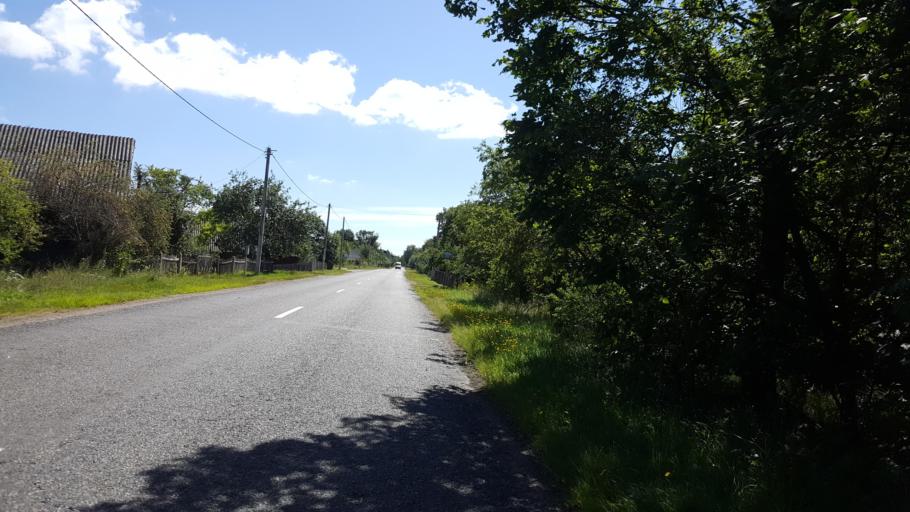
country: BY
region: Brest
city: Zhabinka
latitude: 52.3668
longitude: 24.1436
